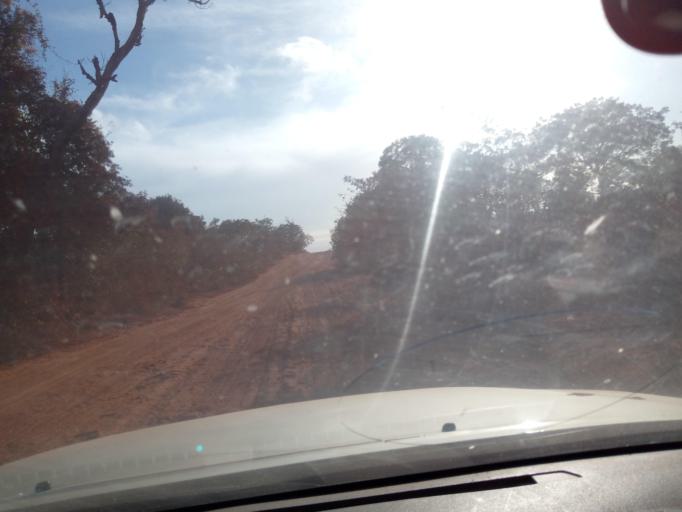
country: ML
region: Sikasso
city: Sikasso
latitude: 11.4260
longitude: -5.5599
